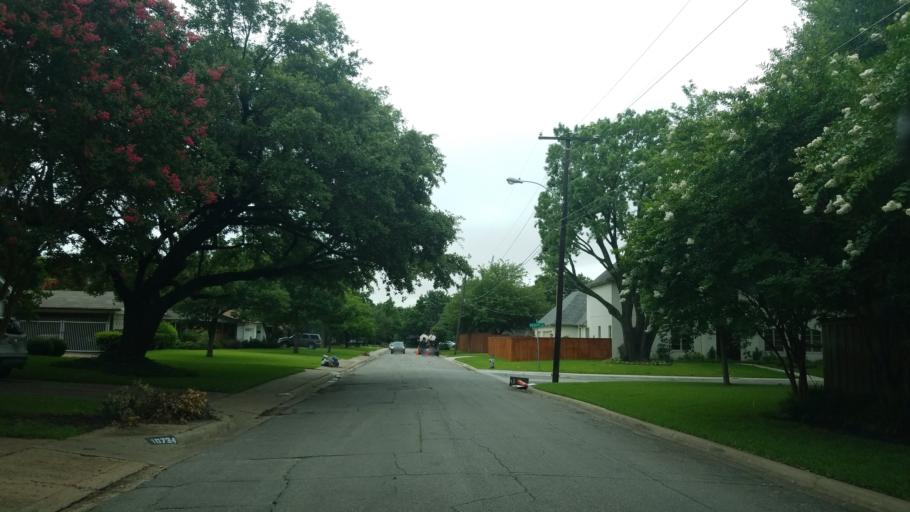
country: US
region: Texas
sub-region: Dallas County
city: Farmers Branch
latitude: 32.8945
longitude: -96.8574
